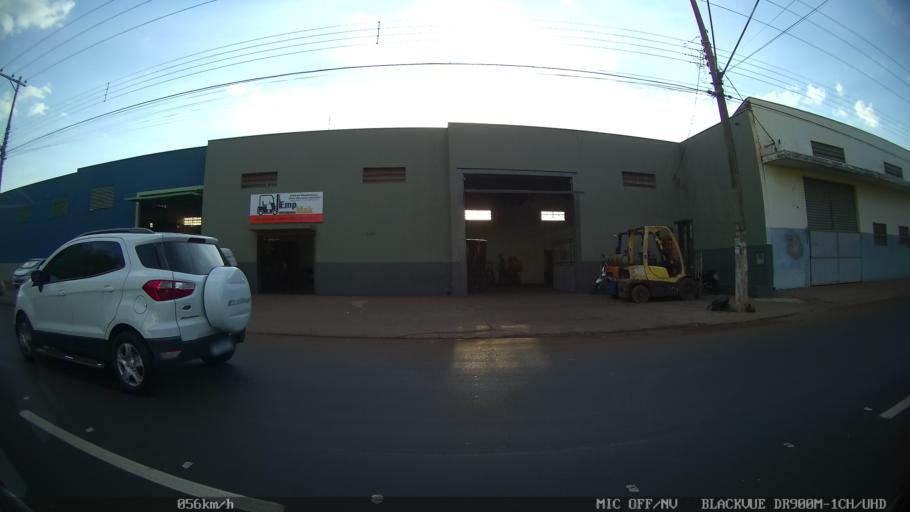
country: BR
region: Sao Paulo
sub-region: Ribeirao Preto
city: Ribeirao Preto
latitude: -21.1317
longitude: -47.7944
